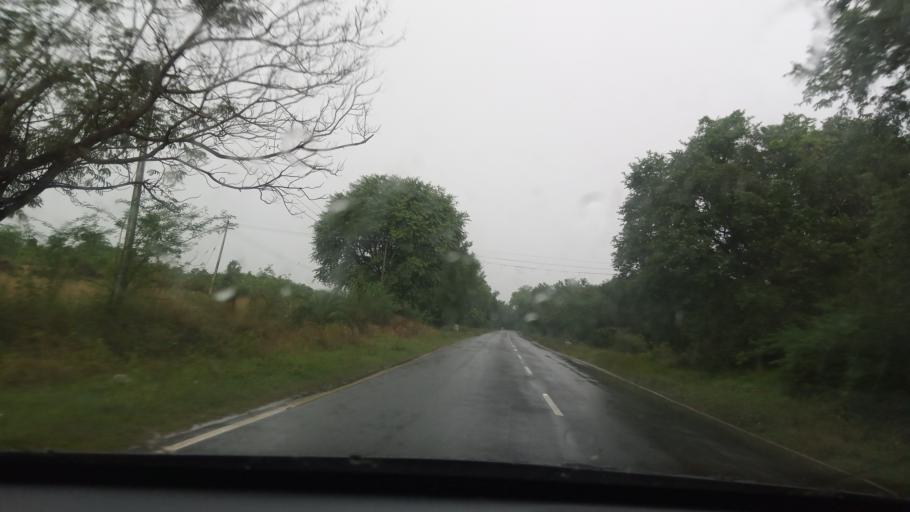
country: IN
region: Tamil Nadu
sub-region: Vellore
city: Kalavai
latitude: 12.8246
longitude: 79.4080
